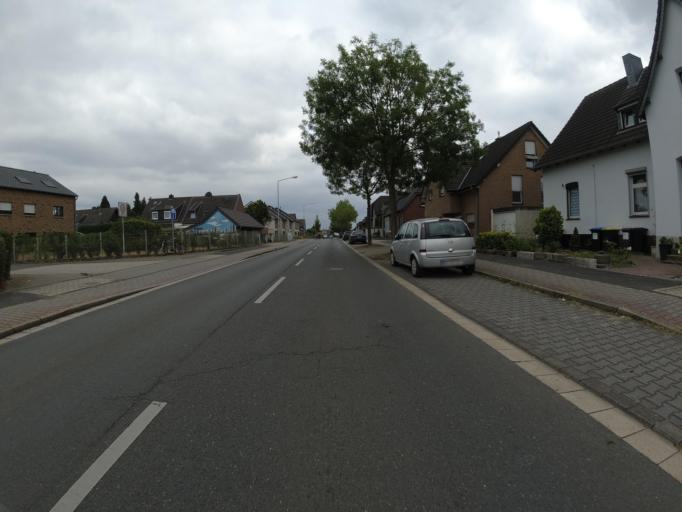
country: DE
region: North Rhine-Westphalia
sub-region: Regierungsbezirk Dusseldorf
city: Moers
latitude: 51.4574
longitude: 6.6609
